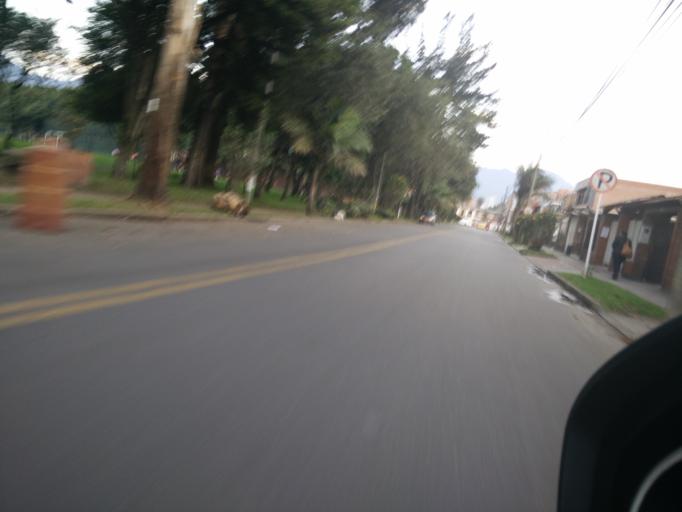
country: CO
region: Bogota D.C.
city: Bogota
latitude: 4.6461
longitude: -74.0907
